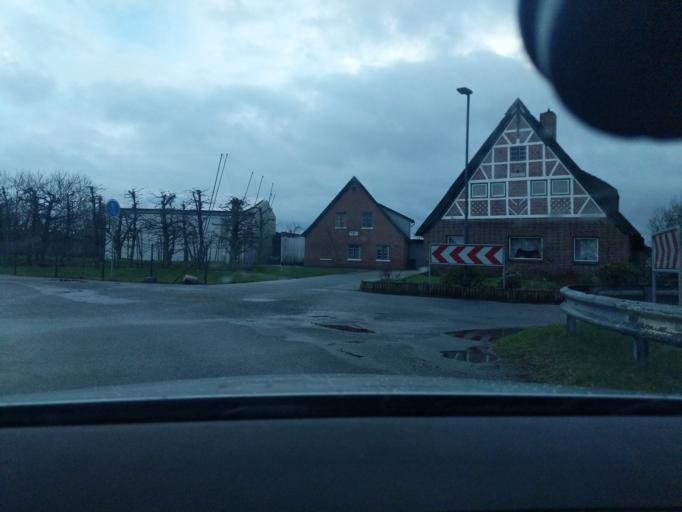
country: DE
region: Lower Saxony
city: Jork
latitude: 53.5339
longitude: 9.6517
